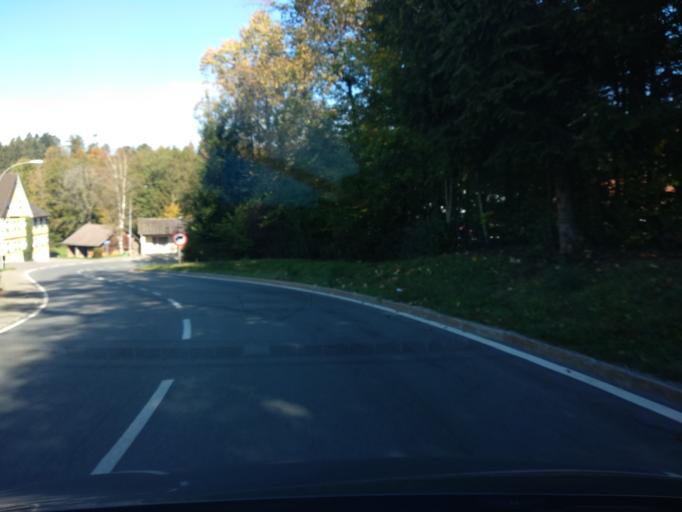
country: AT
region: Vorarlberg
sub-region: Politischer Bezirk Bregenz
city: Hohenweiler
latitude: 47.5941
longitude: 9.7793
